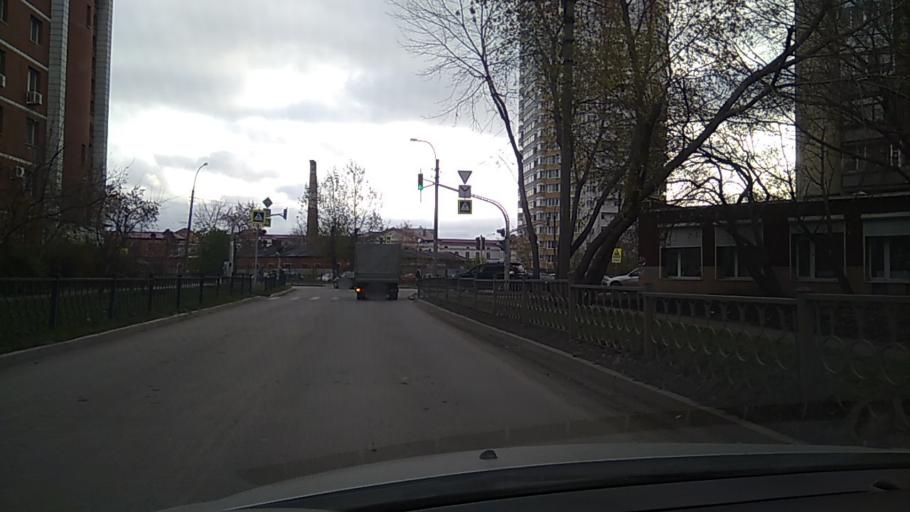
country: RU
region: Sverdlovsk
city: Yekaterinburg
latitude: 56.8541
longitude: 60.5821
